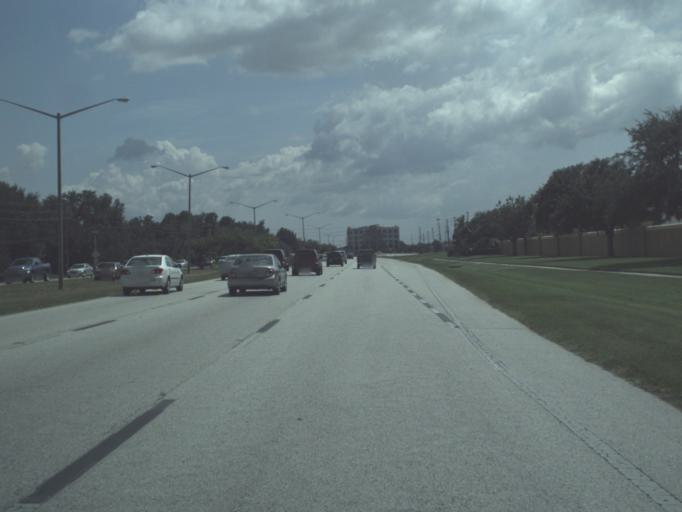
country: US
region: Florida
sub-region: Pinellas County
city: Saint George
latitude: 28.0736
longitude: -82.7043
